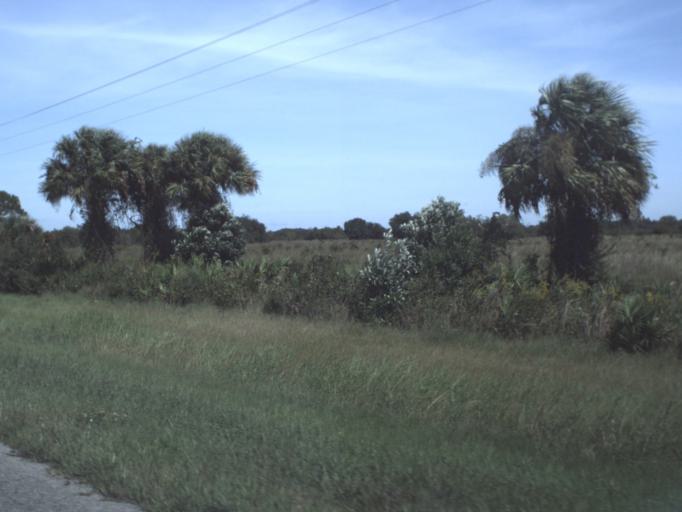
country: US
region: Florida
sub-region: Hendry County
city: Port LaBelle
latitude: 26.9812
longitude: -81.3212
